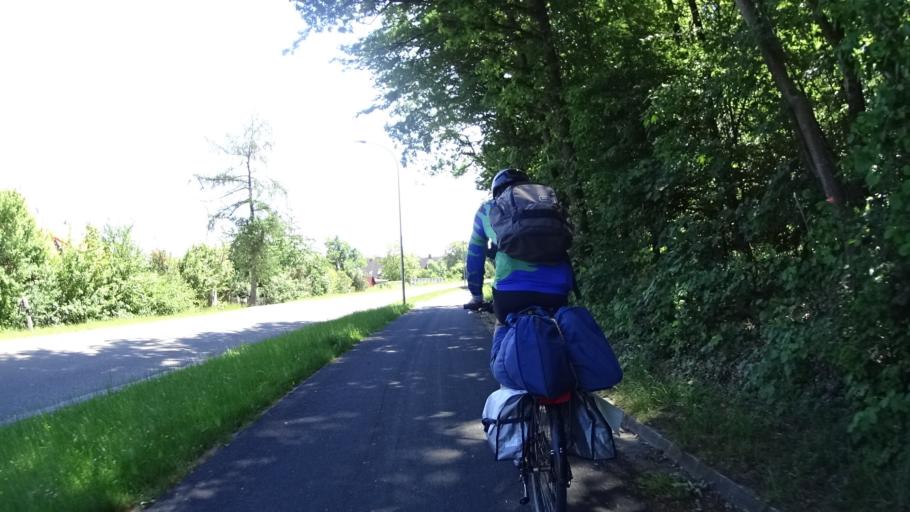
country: DE
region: Bavaria
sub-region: Regierungsbezirk Mittelfranken
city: Gunzenhausen
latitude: 49.1202
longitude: 10.7896
